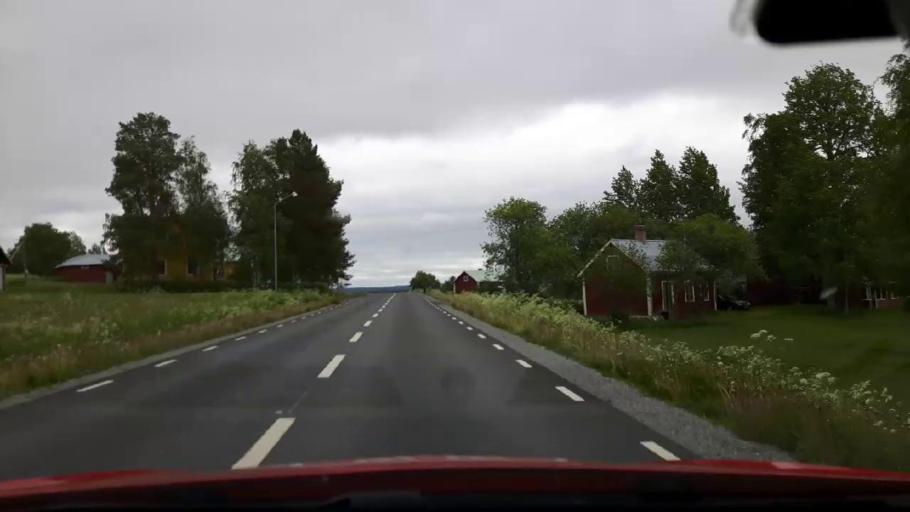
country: SE
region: Jaemtland
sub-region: OEstersunds Kommun
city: Lit
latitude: 63.7390
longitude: 14.8610
